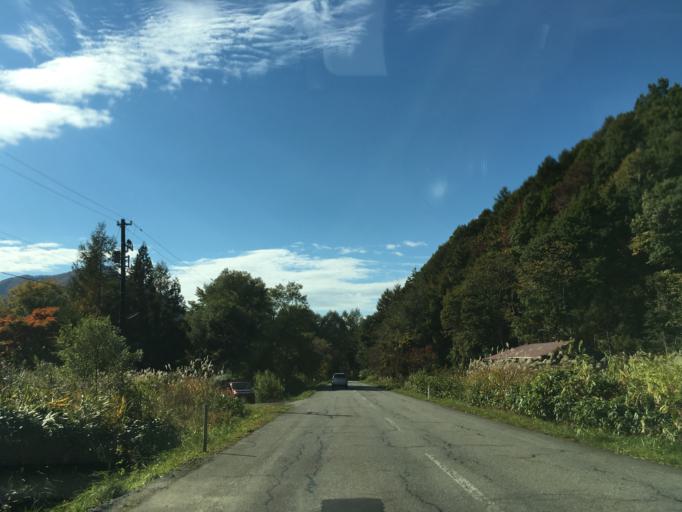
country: JP
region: Fukushima
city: Inawashiro
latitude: 37.6514
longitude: 140.1685
